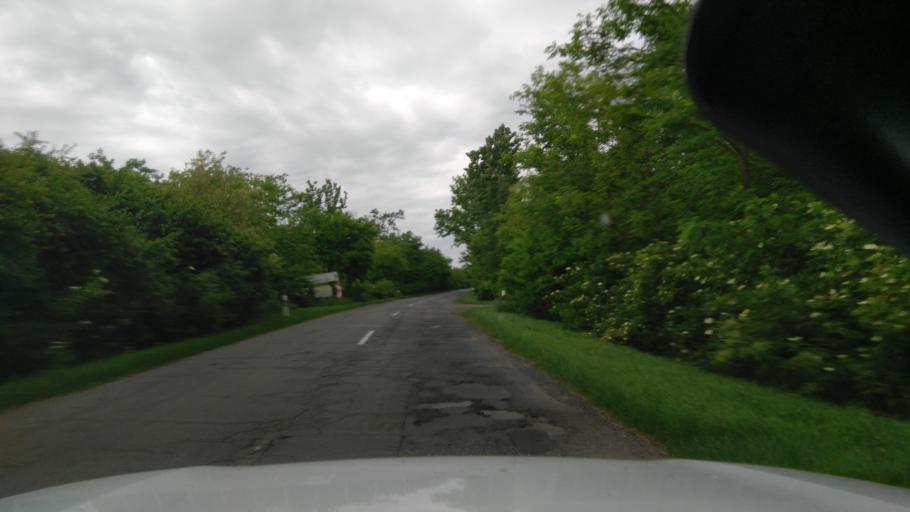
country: HU
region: Bekes
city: Bekescsaba
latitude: 46.6814
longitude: 21.1670
